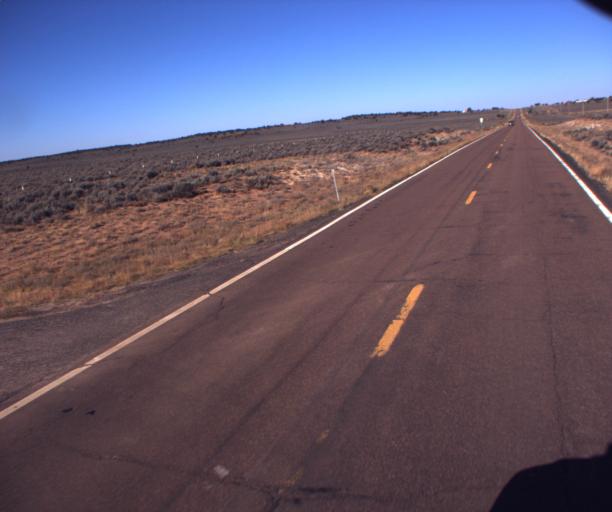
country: US
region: Arizona
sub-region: Apache County
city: Ganado
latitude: 35.7535
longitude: -109.9474
